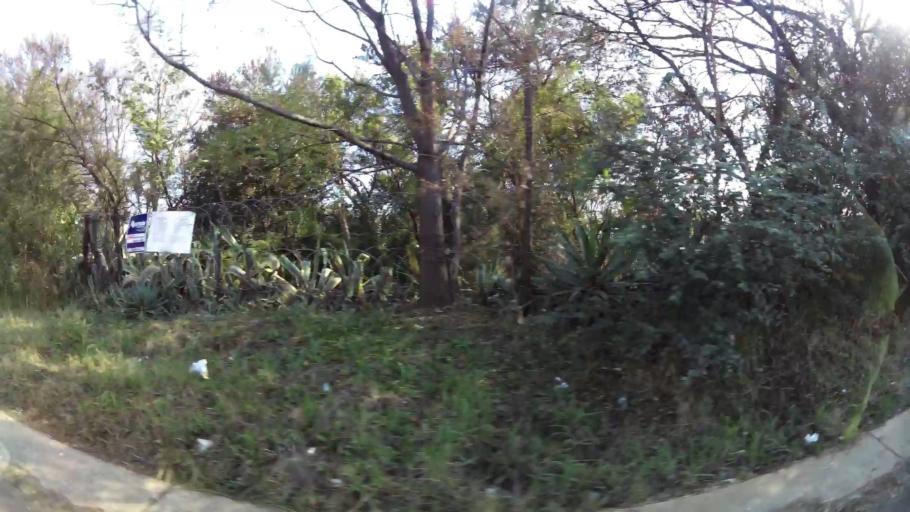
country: ZA
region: Gauteng
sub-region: City of Tshwane Metropolitan Municipality
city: Pretoria
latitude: -25.7557
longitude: 28.3314
